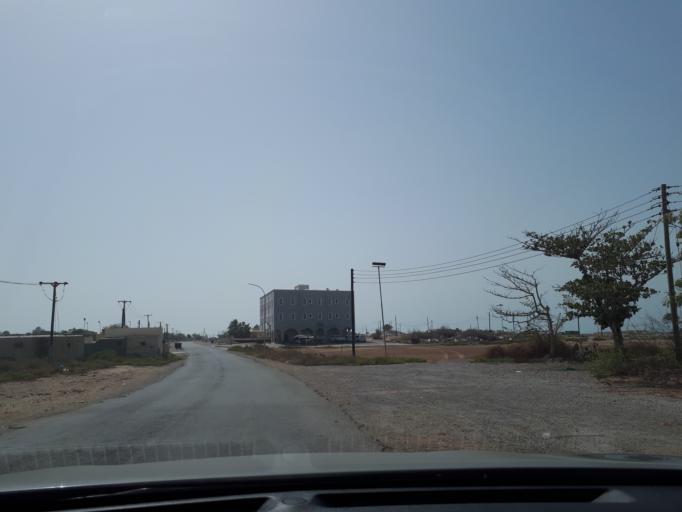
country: OM
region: Al Batinah
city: Barka'
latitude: 23.7071
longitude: 57.9110
